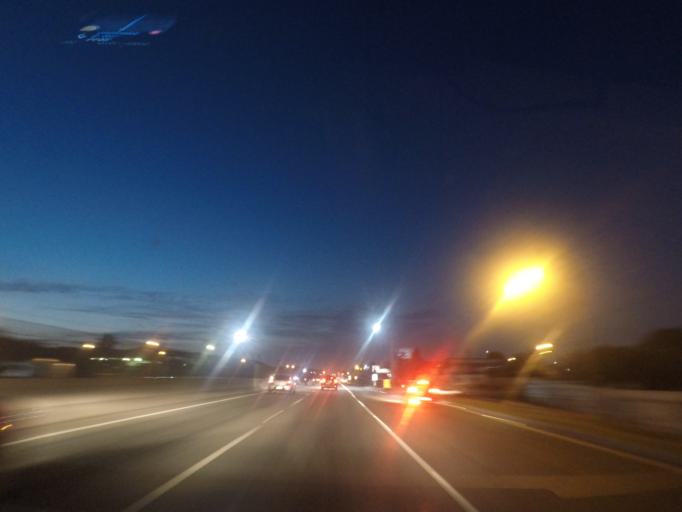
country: BR
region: Parana
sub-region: Pinhais
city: Pinhais
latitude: -25.4644
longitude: -49.2169
